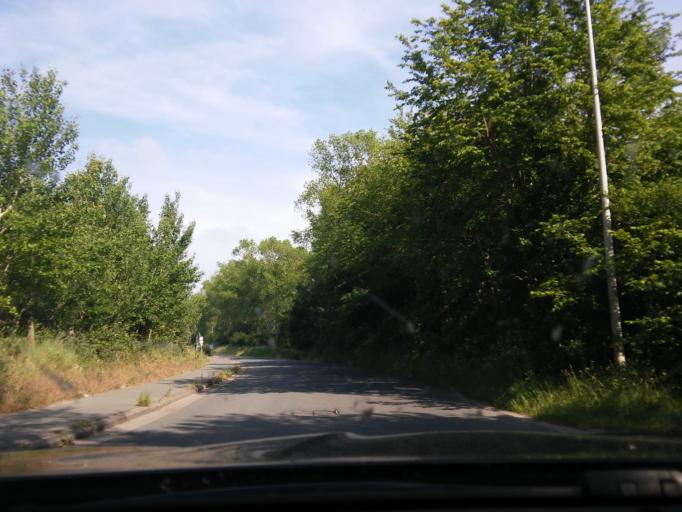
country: BE
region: Flanders
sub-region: Provincie West-Vlaanderen
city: Knokke-Heist
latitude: 51.3460
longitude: 3.3318
